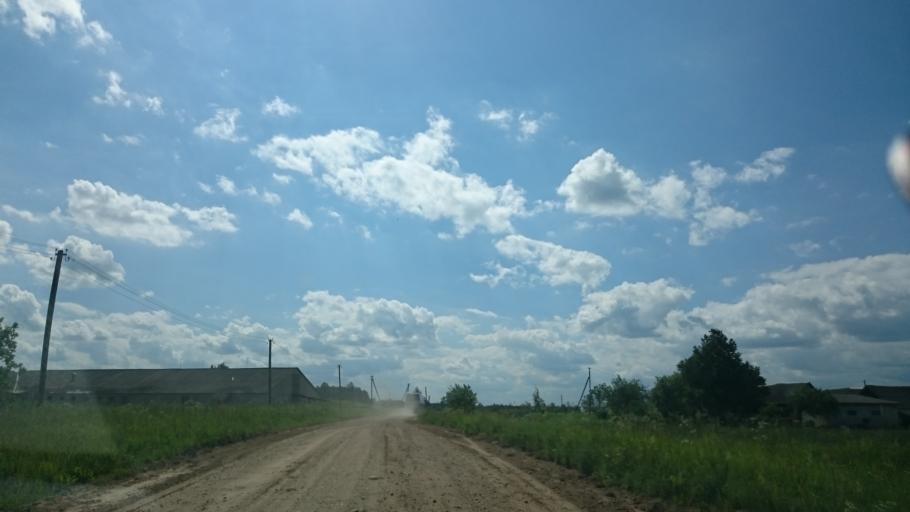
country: LV
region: Cibla
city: Cibla
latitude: 56.6316
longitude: 27.8733
